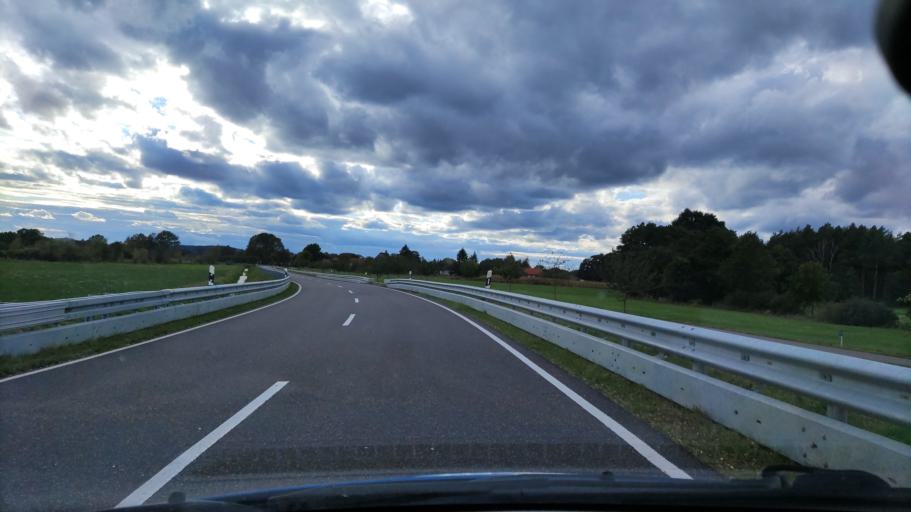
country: DE
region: Lower Saxony
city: Hitzacker
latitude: 53.1824
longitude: 11.0896
